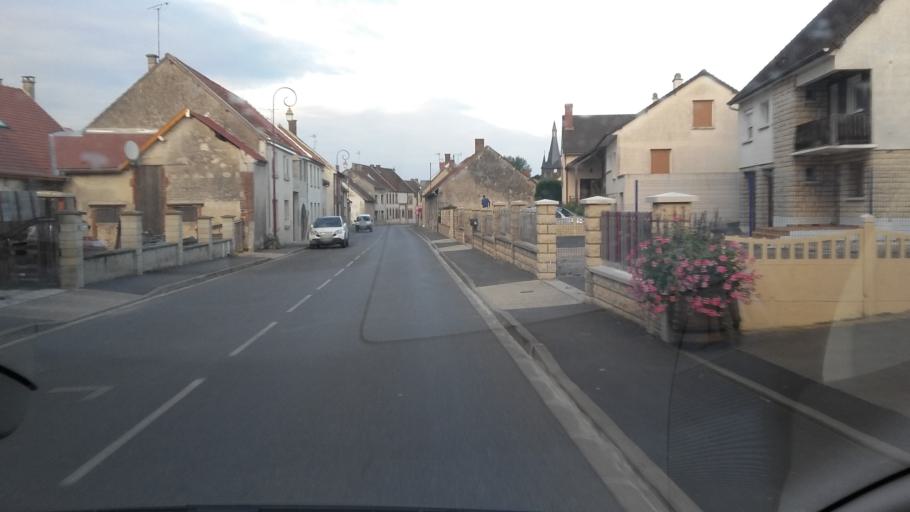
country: FR
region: Champagne-Ardenne
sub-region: Departement de la Marne
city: Vertus
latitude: 48.8782
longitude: 4.0016
